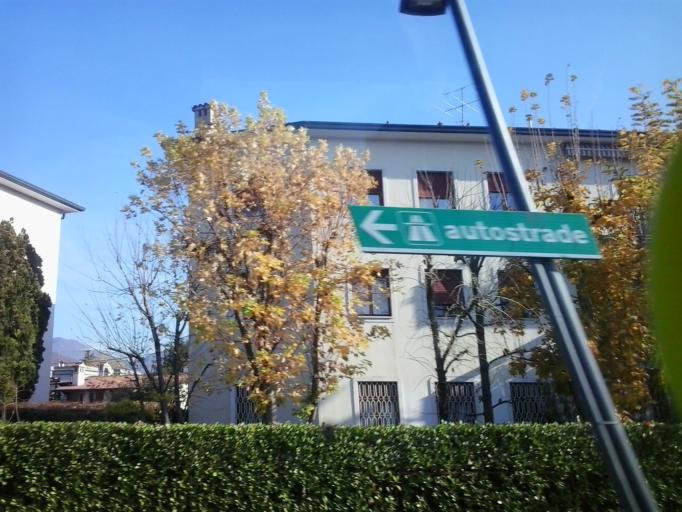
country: IT
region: Lombardy
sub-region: Provincia di Brescia
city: Brescia
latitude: 45.5597
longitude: 10.2338
